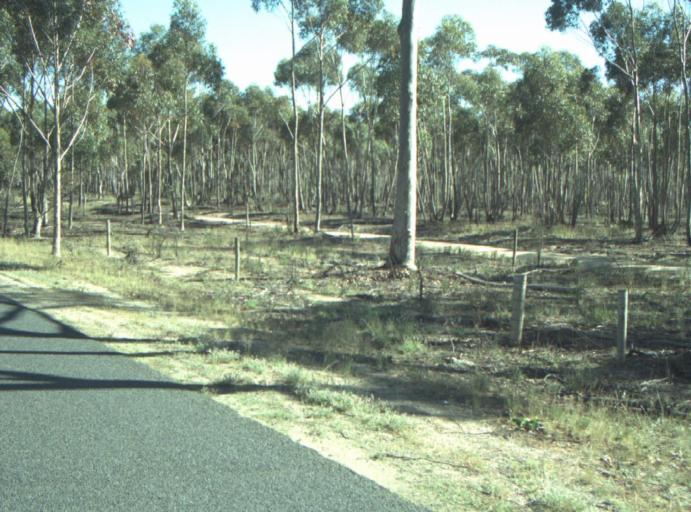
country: AU
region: Victoria
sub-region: Greater Geelong
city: Lara
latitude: -37.9610
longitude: 144.4030
